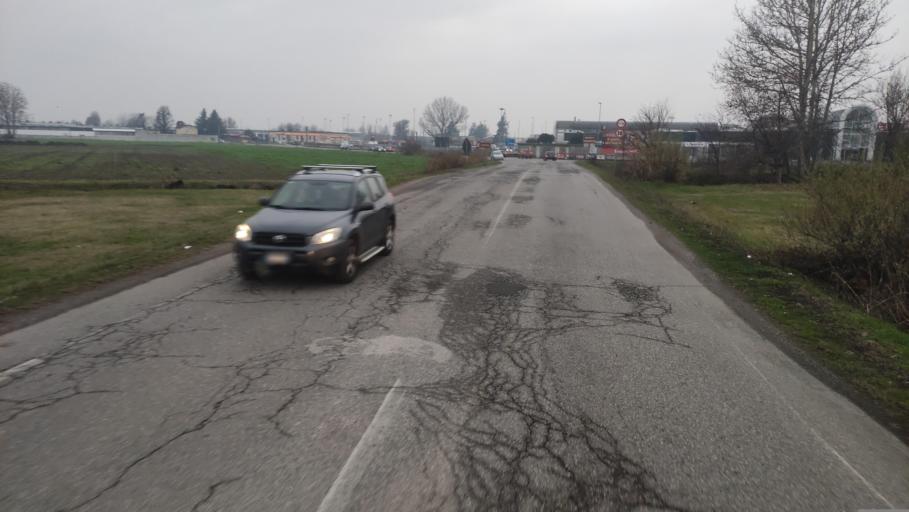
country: IT
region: Lombardy
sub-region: Provincia di Cremona
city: Bagnolo Cremasco
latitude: 45.3624
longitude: 9.6339
